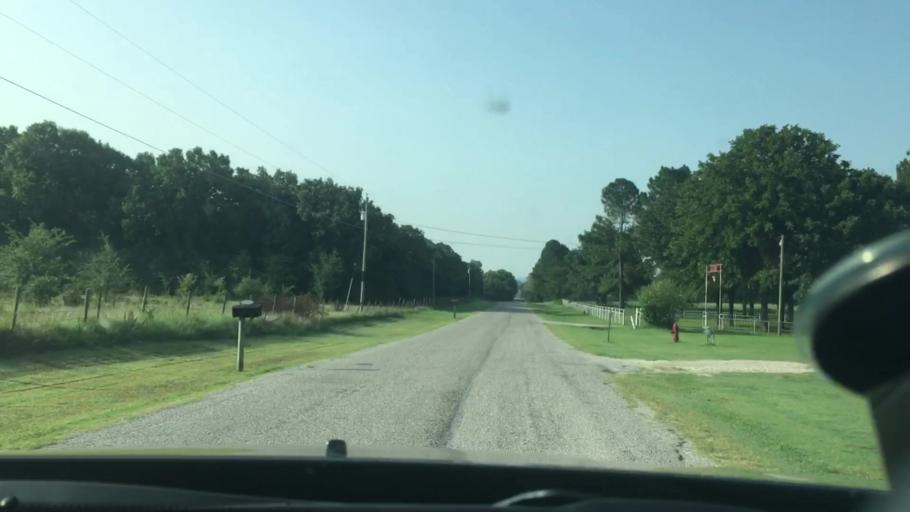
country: US
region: Oklahoma
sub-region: Pontotoc County
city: Ada
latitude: 34.7954
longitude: -96.7397
